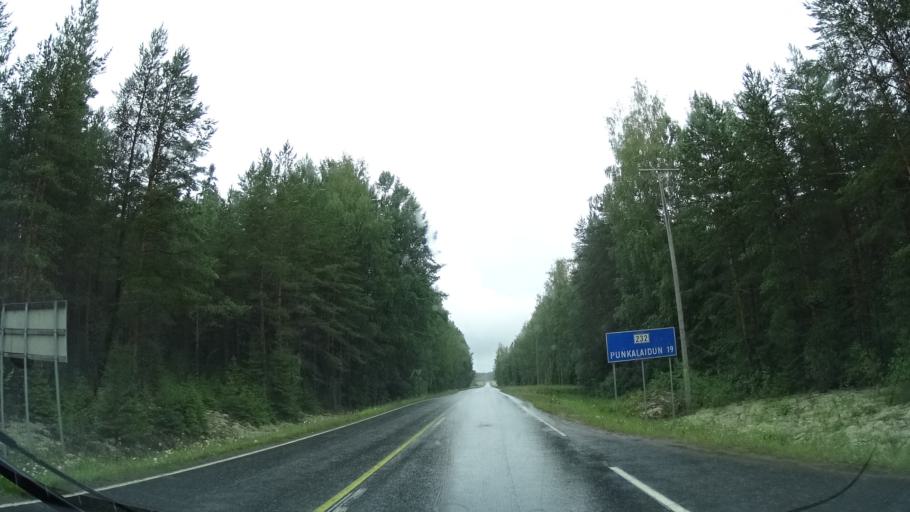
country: FI
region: Haeme
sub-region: Forssa
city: Humppila
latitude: 60.9759
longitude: 23.2526
